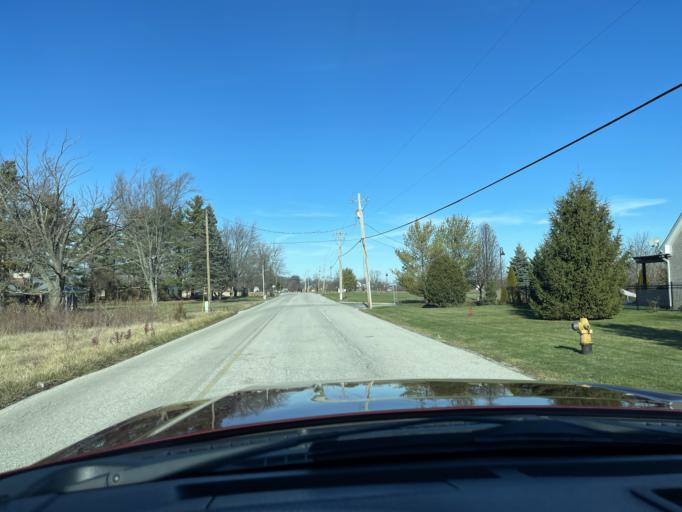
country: US
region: Indiana
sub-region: Hendricks County
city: Avon
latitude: 39.7586
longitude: -86.4572
